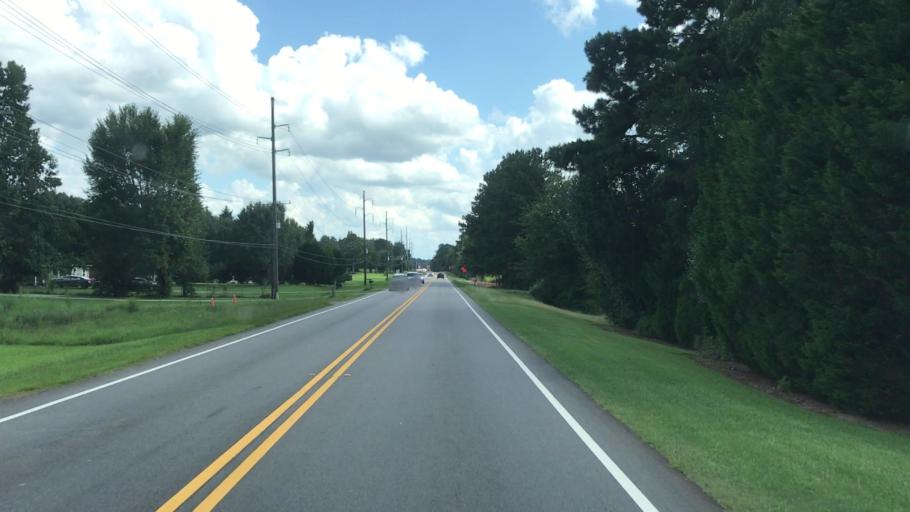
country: US
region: Georgia
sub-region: Newton County
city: Oxford
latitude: 33.6439
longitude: -83.8353
